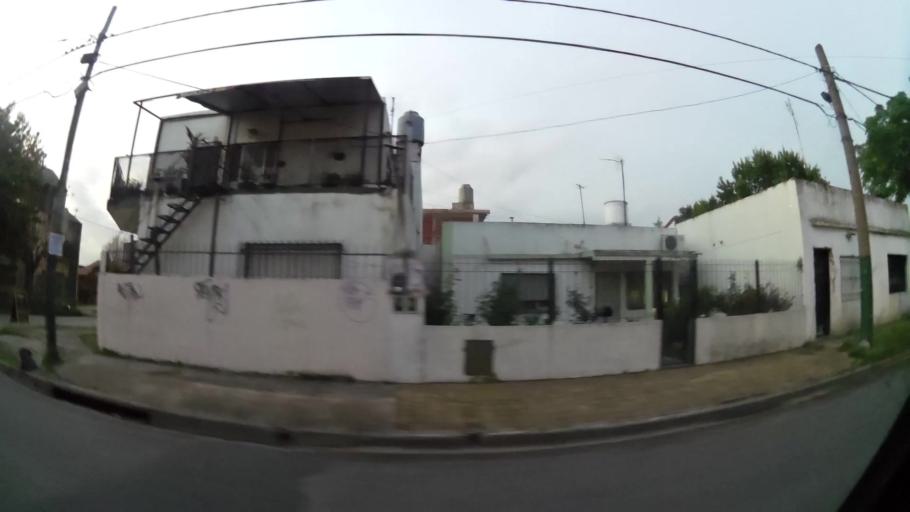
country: AR
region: Buenos Aires
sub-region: Partido de Lomas de Zamora
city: Lomas de Zamora
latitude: -34.7509
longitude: -58.3664
